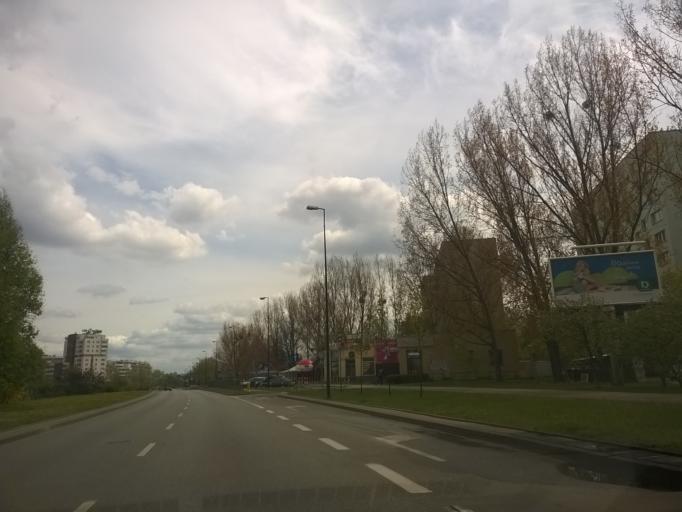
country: PL
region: Masovian Voivodeship
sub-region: Warszawa
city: Ursynow
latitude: 52.1559
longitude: 21.0460
